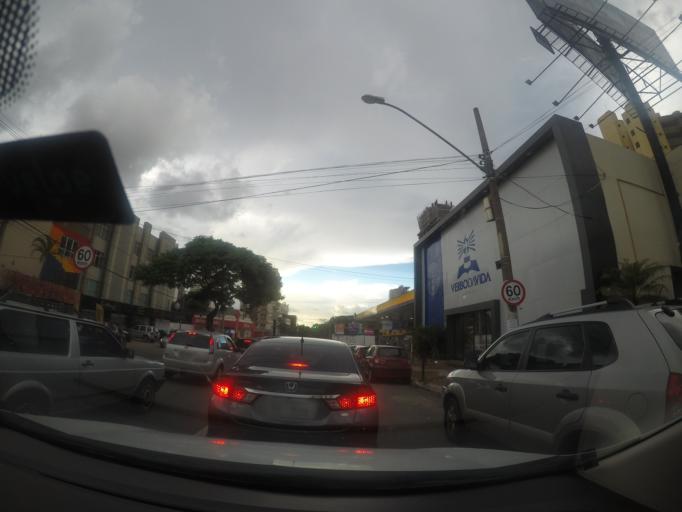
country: BR
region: Goias
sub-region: Goiania
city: Goiania
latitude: -16.7016
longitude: -49.2707
